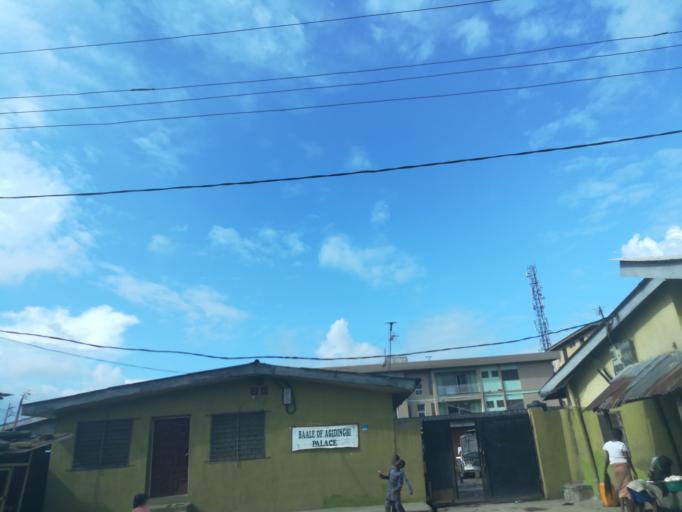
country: NG
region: Lagos
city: Agege
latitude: 6.6244
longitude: 3.3513
